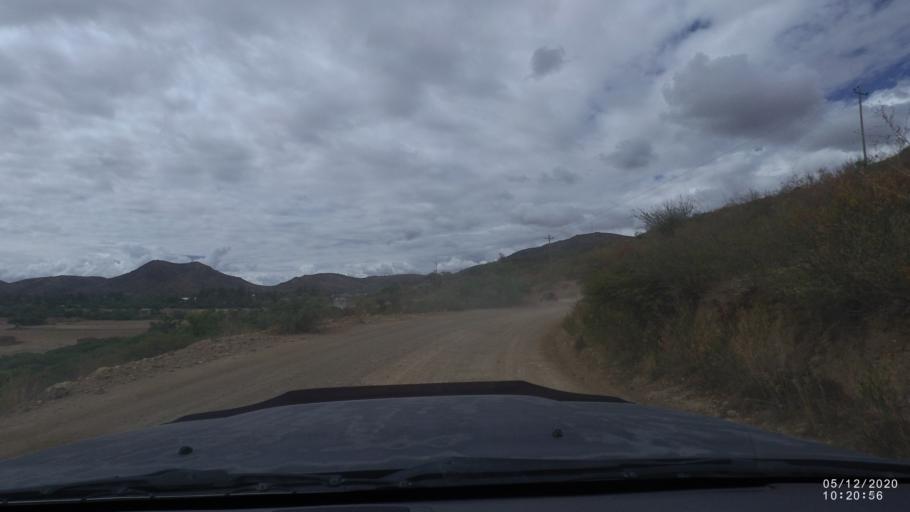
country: BO
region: Cochabamba
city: Sipe Sipe
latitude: -17.4864
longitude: -66.2824
